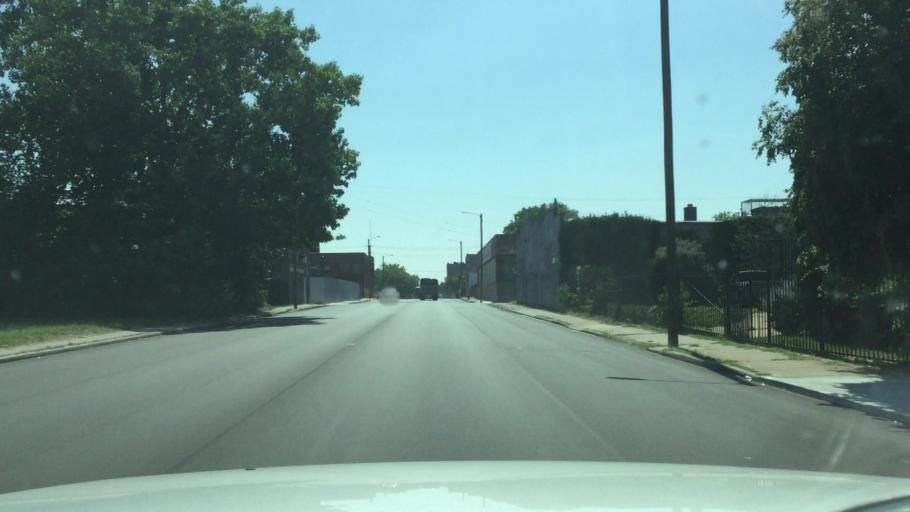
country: US
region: Michigan
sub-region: Wayne County
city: Detroit
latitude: 42.3631
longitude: -83.0166
